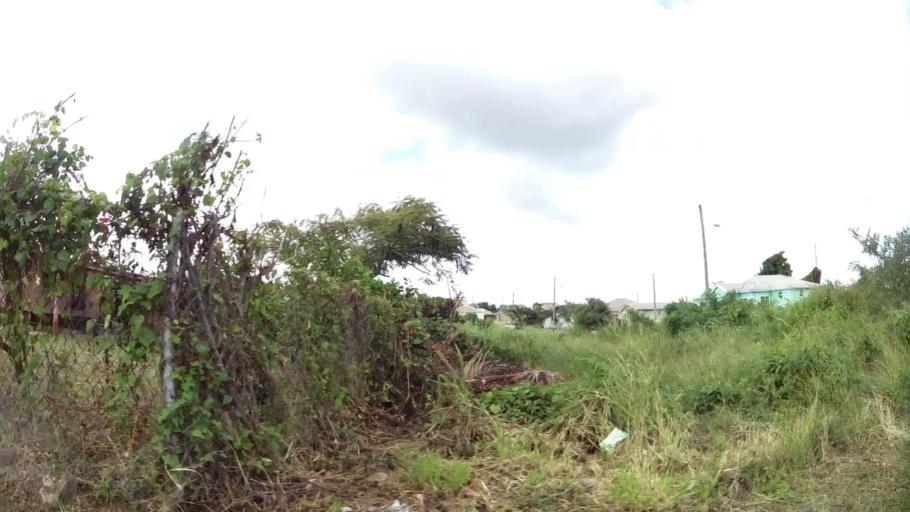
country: AG
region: Saint John
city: Saint John's
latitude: 17.1110
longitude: -61.8545
